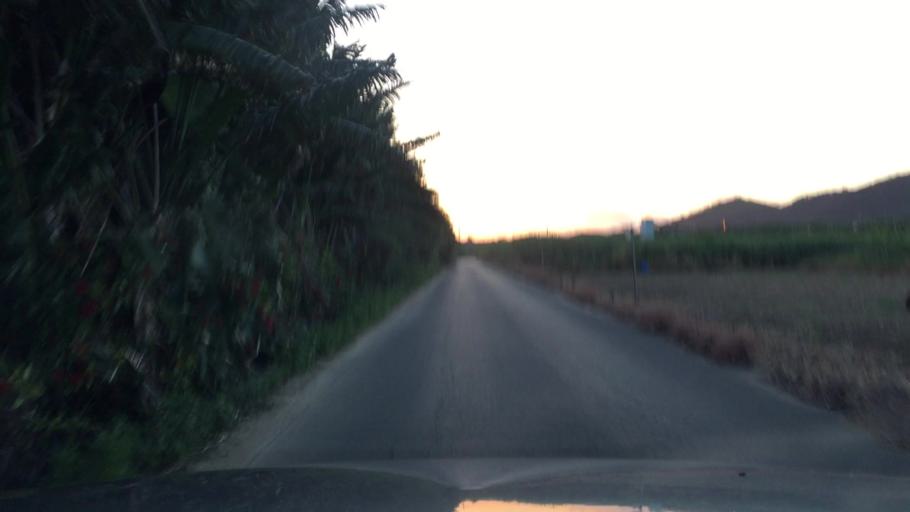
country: JP
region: Okinawa
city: Ishigaki
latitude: 24.3555
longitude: 124.1601
